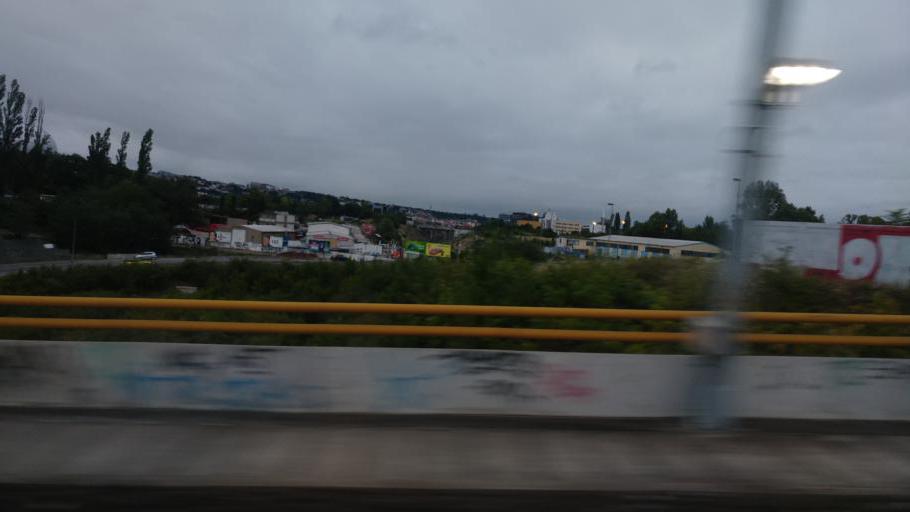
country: CZ
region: Praha
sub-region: Praha 8
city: Liben
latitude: 50.0983
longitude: 14.4738
